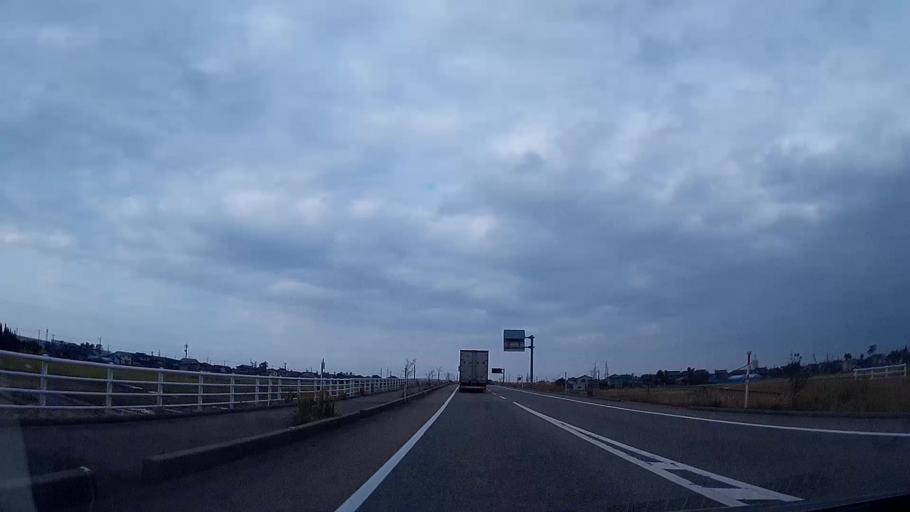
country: JP
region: Toyama
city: Nyuzen
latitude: 36.8943
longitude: 137.4444
